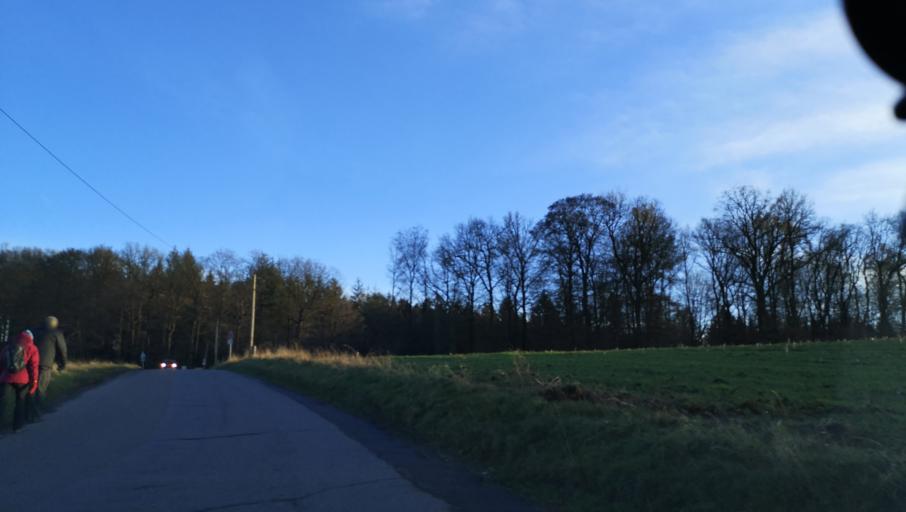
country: DE
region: North Rhine-Westphalia
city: Radevormwald
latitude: 51.1669
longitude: 7.3905
